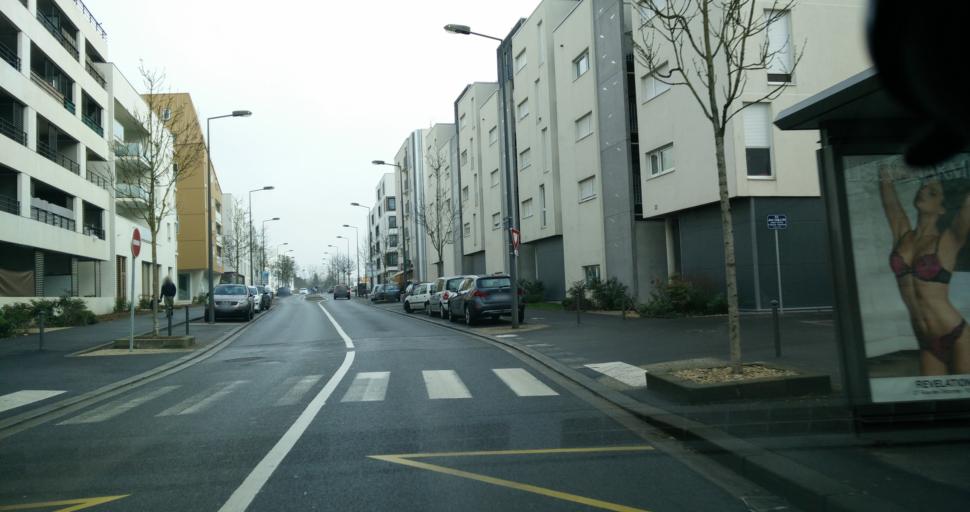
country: FR
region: Centre
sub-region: Departement d'Indre-et-Loire
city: Saint-Cyr-sur-Loire
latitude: 47.4185
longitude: 0.6944
